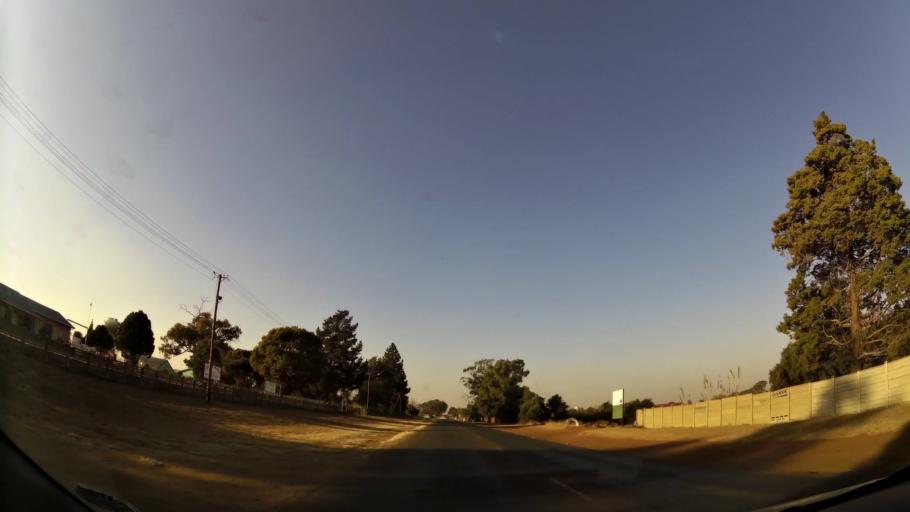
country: ZA
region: Gauteng
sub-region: West Rand District Municipality
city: Randfontein
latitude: -26.2193
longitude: 27.6441
